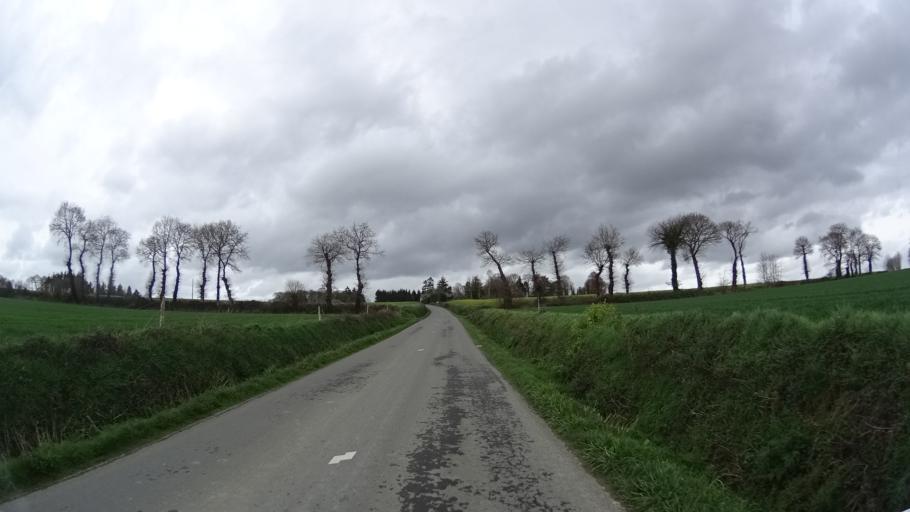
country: FR
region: Brittany
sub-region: Departement d'Ille-et-Vilaine
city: Saint-Gilles
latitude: 48.1734
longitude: -1.8294
